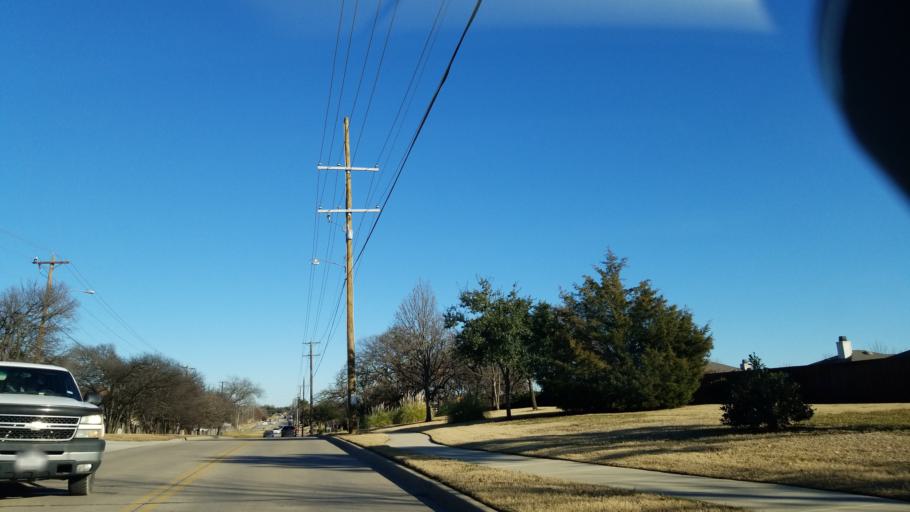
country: US
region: Texas
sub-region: Denton County
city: Corinth
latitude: 33.1583
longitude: -97.0994
